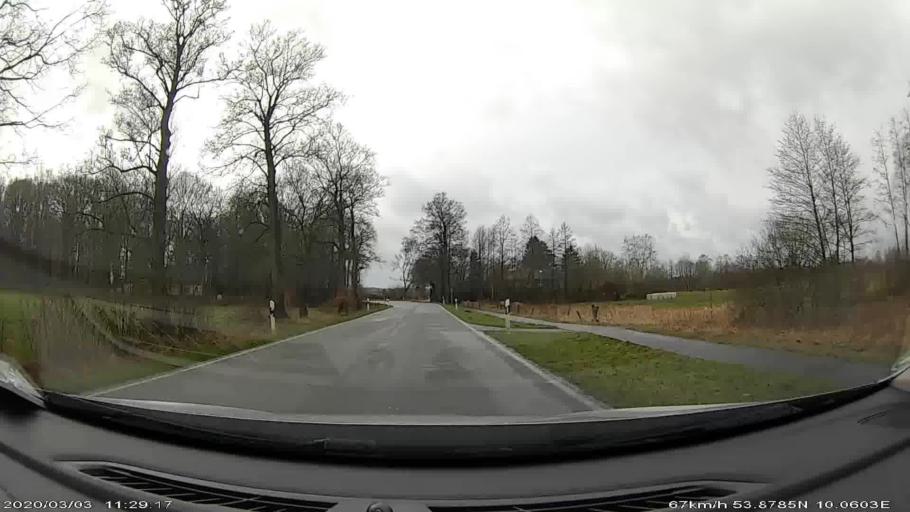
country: DE
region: Schleswig-Holstein
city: Struvenhutten
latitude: 53.8763
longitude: 10.0595
